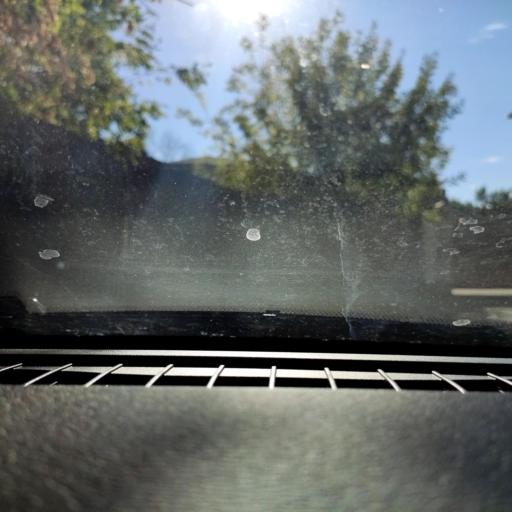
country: RU
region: Voronezj
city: Voronezh
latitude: 51.7229
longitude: 39.2284
